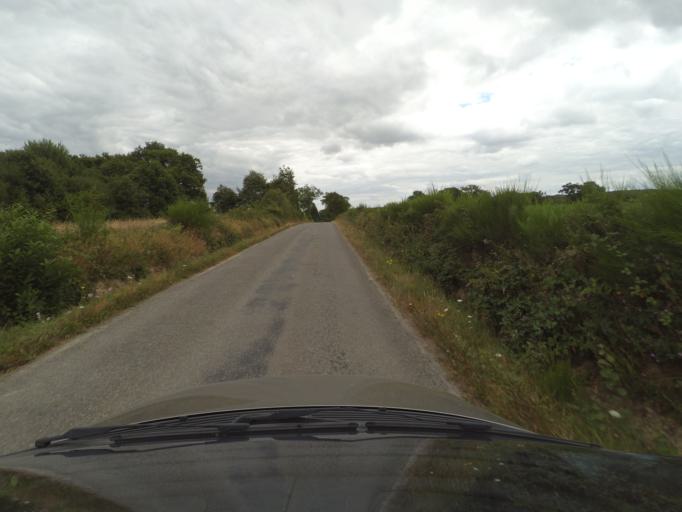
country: FR
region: Limousin
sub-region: Departement de la Haute-Vienne
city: Arnac-la-Poste
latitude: 46.2722
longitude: 1.2819
